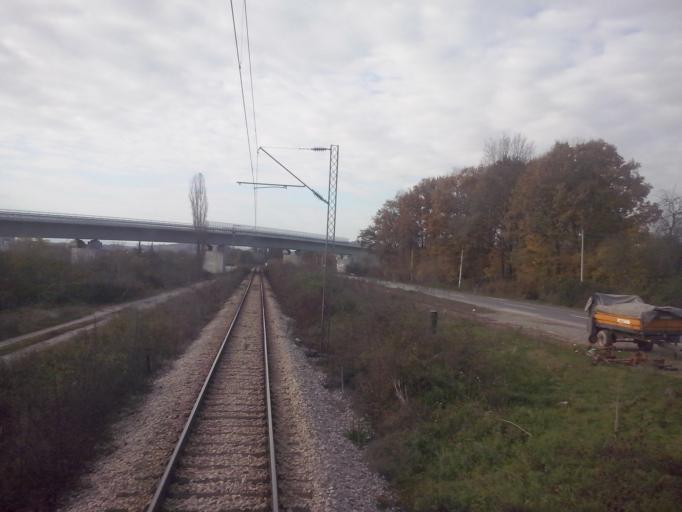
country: RS
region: Central Serbia
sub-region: Kolubarski Okrug
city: Lajkovac
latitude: 44.3621
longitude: 20.1206
